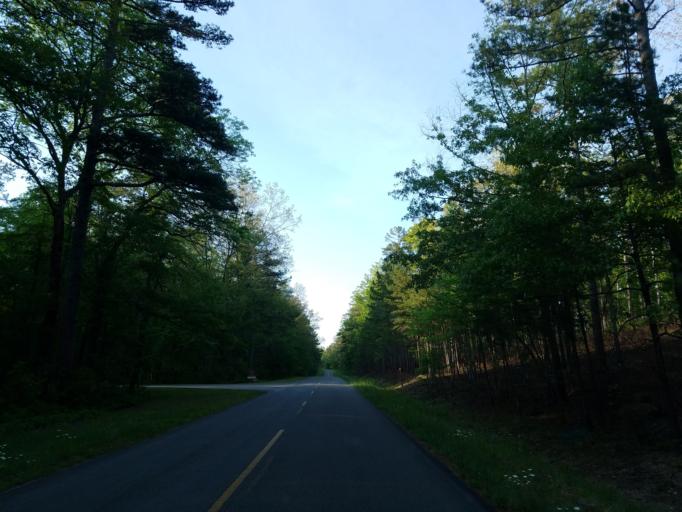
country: US
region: Georgia
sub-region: Gordon County
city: Calhoun
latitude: 34.6128
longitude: -85.0809
